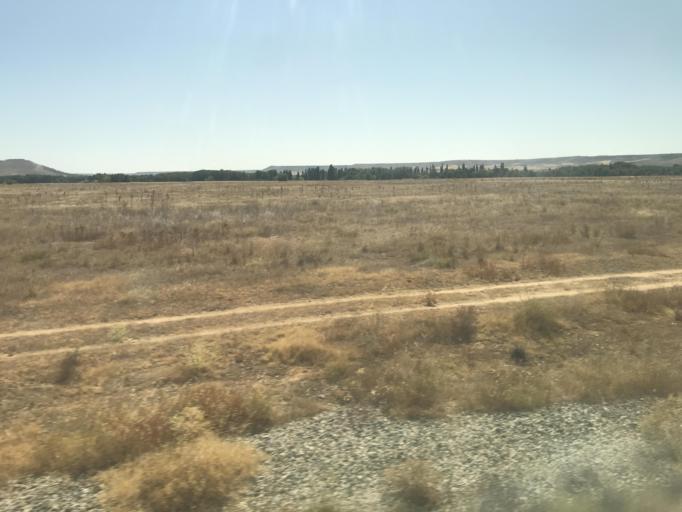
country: ES
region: Castille and Leon
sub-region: Provincia de Valladolid
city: Cubillas de Santa Marta
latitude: 41.8229
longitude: -4.5706
